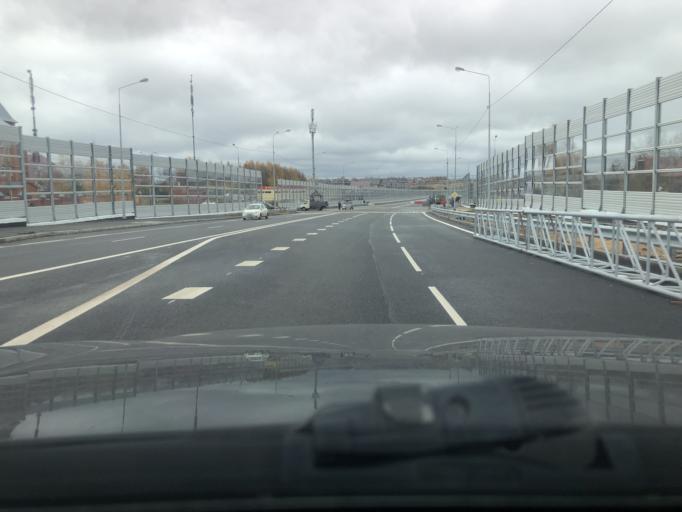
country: RU
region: Moskovskaya
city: Sergiyev Posad
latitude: 56.3083
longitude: 38.0991
